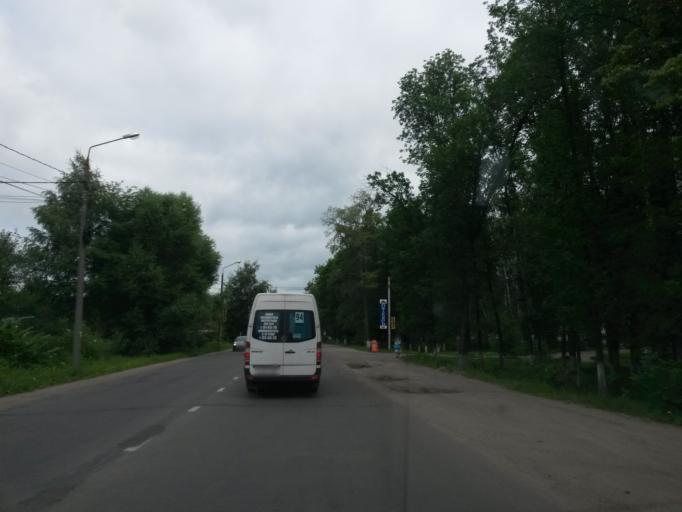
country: RU
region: Jaroslavl
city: Yaroslavl
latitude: 57.5900
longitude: 39.8772
